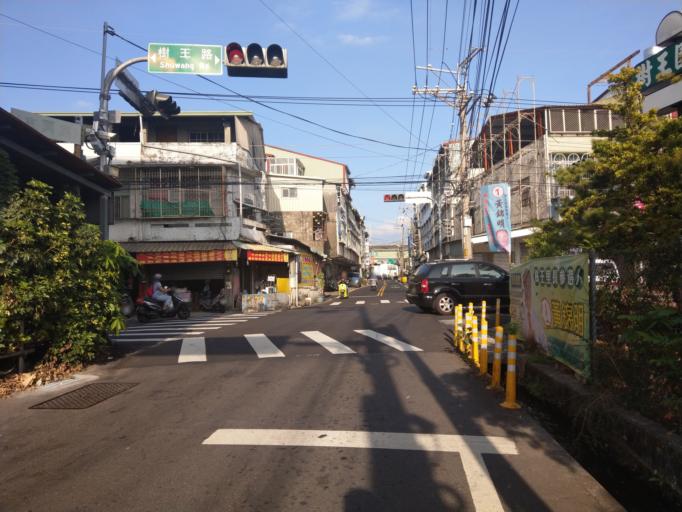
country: TW
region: Taiwan
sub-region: Taichung City
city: Taichung
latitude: 24.1071
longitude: 120.6701
